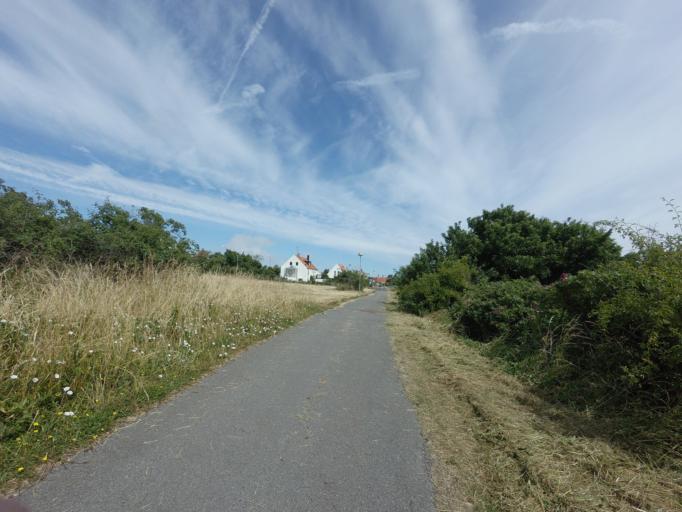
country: SE
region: Skane
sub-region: Simrishamns Kommun
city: Simrishamn
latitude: 55.5416
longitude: 14.3564
